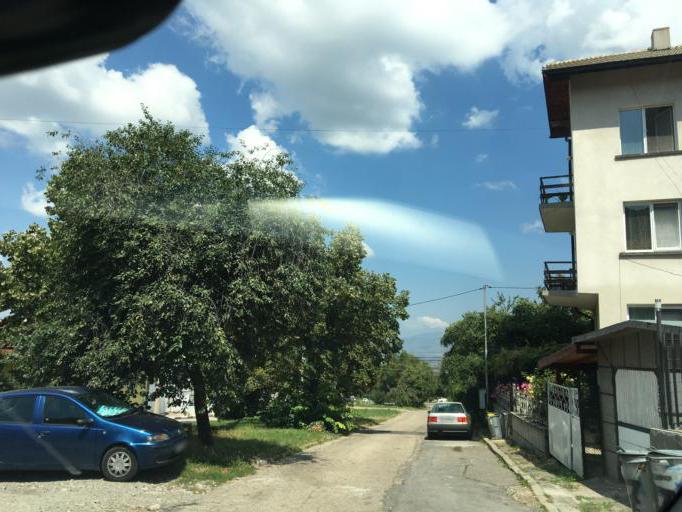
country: BG
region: Sofiya
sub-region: Obshtina Elin Pelin
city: Elin Pelin
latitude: 42.6024
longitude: 23.4725
